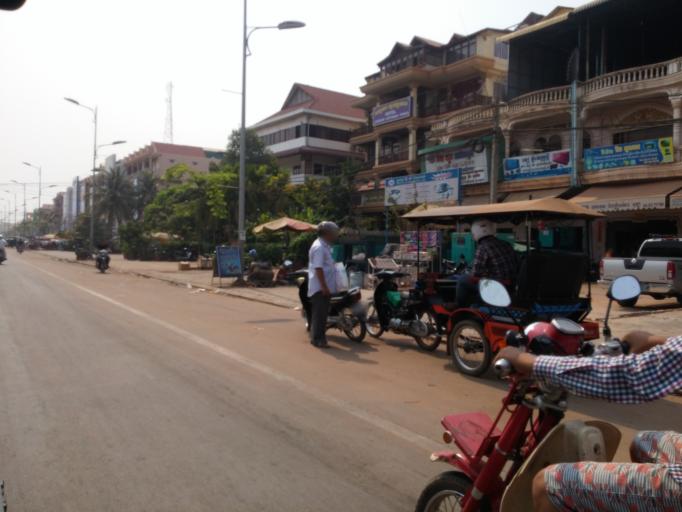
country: KH
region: Siem Reap
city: Siem Reap
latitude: 13.3611
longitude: 103.8698
